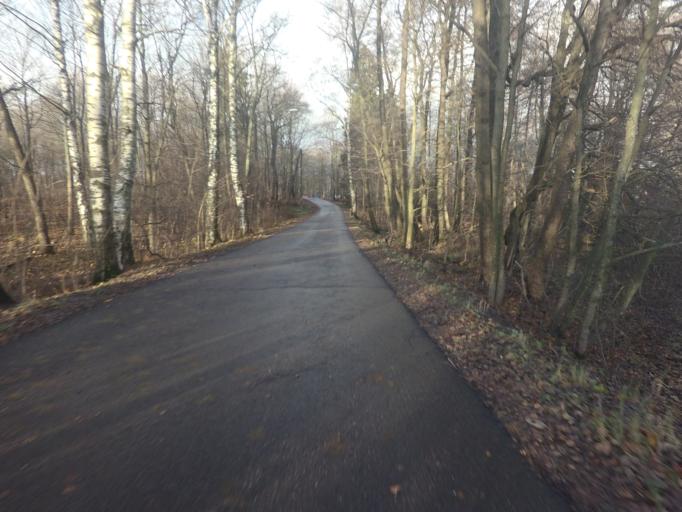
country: FI
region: Uusimaa
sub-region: Helsinki
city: Teekkarikylae
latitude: 60.2054
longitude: 24.8416
